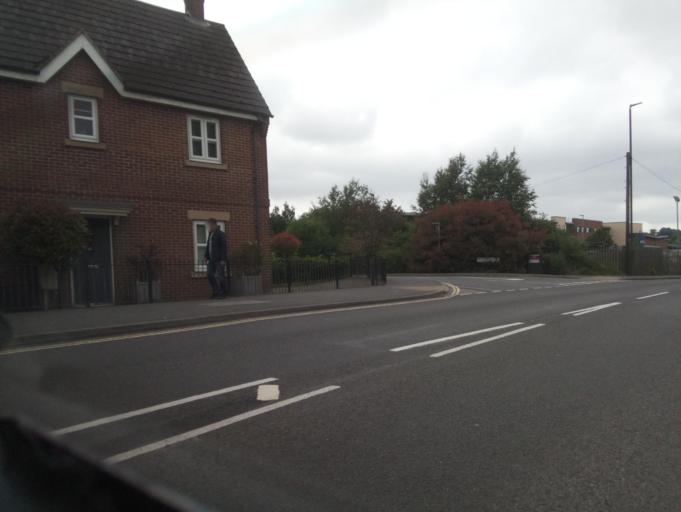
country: GB
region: England
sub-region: Derbyshire
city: Ashbourne
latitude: 53.0115
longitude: -1.7402
